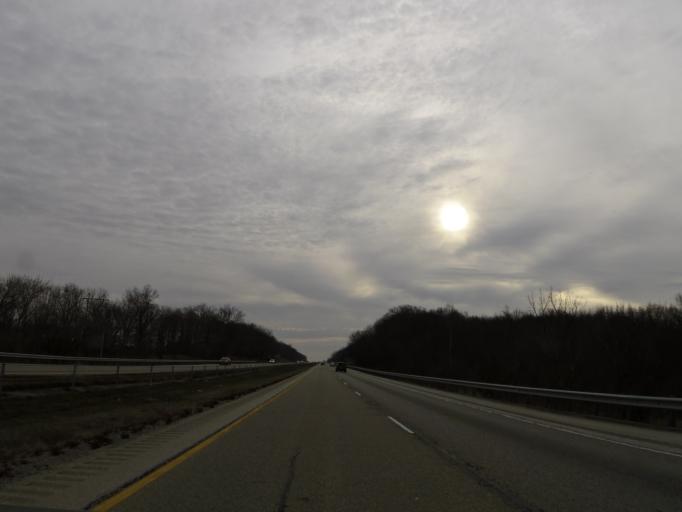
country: US
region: Illinois
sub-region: Vermilion County
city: Tilton
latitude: 40.1138
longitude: -87.6914
